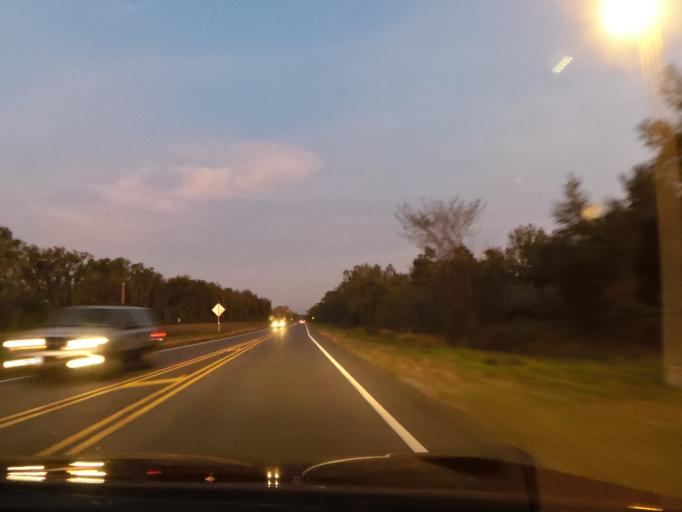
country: US
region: Florida
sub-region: Volusia County
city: De Leon Springs
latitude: 29.2256
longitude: -81.3198
